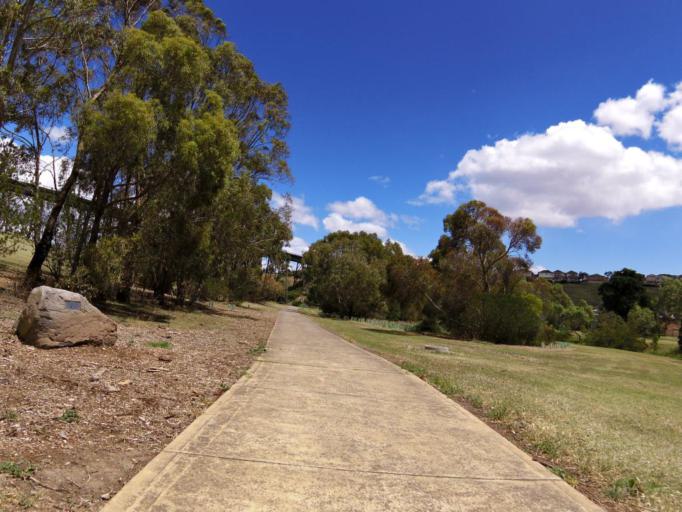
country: AU
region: Victoria
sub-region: Moreland
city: Gowanbrae
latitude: -37.7074
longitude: 144.9004
